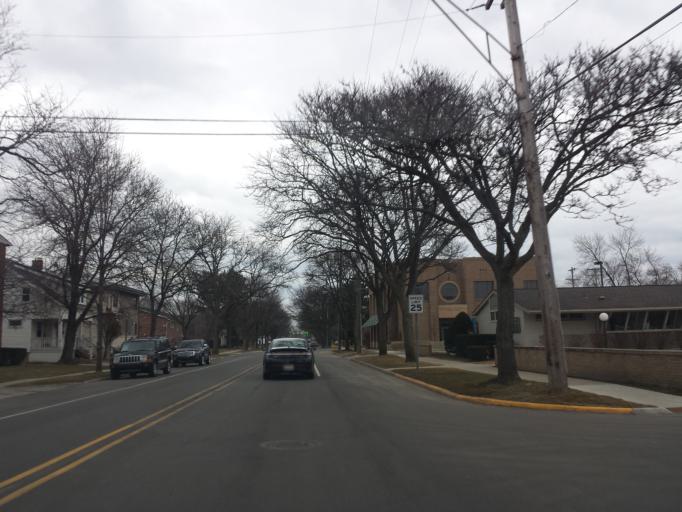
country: US
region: Michigan
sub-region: Oakland County
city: Birmingham
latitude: 42.5390
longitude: -83.2110
